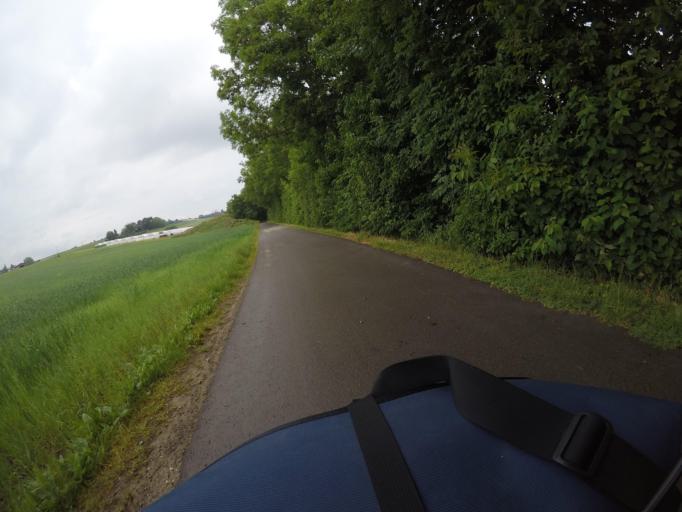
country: DE
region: Baden-Wuerttemberg
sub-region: Regierungsbezirk Stuttgart
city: Ditzingen
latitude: 48.8347
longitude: 9.0602
